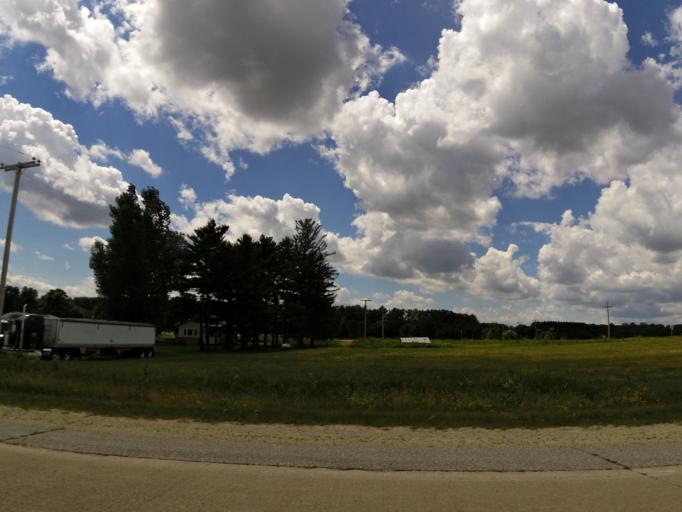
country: US
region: Iowa
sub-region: Fayette County
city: Oelwein
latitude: 42.6049
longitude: -91.9030
